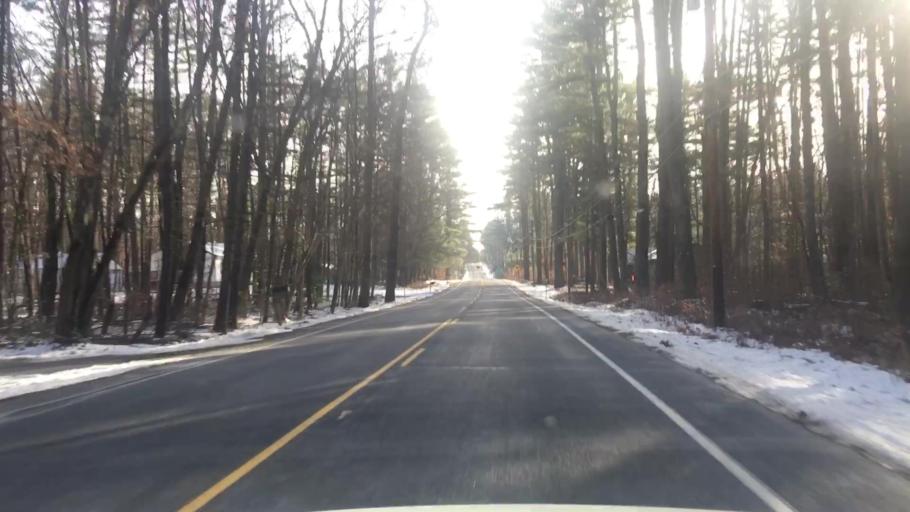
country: US
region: New Hampshire
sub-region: Merrimack County
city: Canterbury
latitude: 43.2933
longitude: -71.5623
